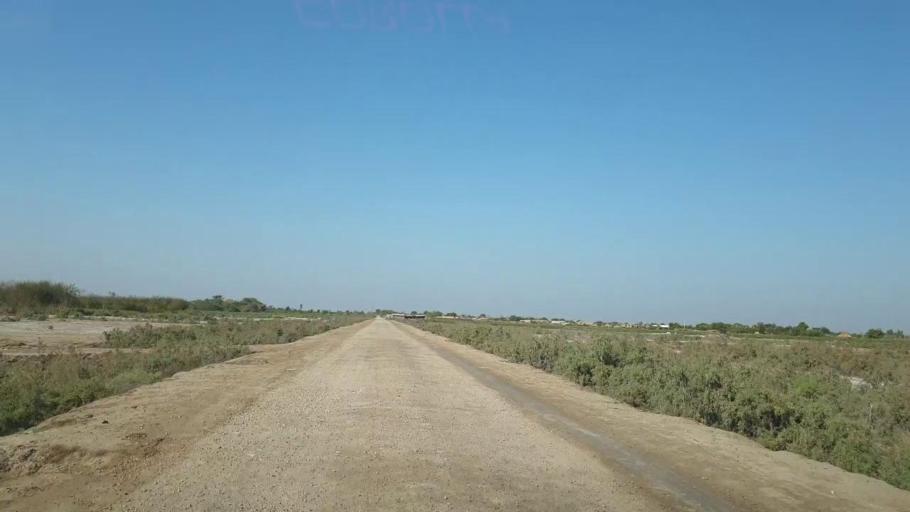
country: PK
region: Sindh
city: Mirpur Khas
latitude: 25.6357
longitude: 69.0588
